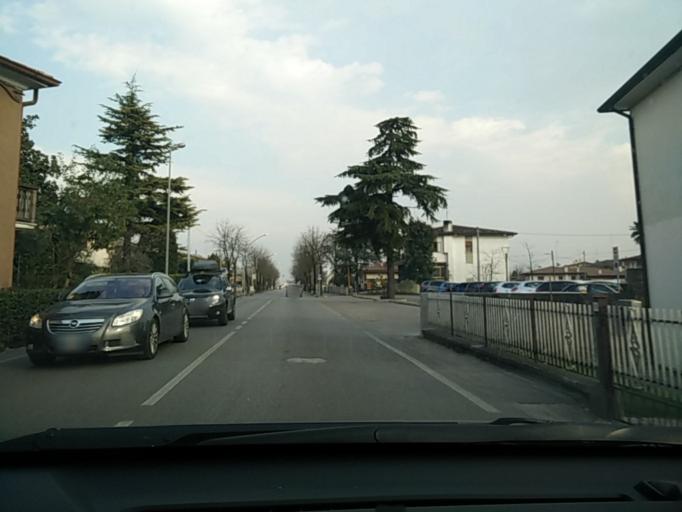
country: IT
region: Veneto
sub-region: Provincia di Treviso
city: San Vendemiano
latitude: 45.8751
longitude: 12.3462
